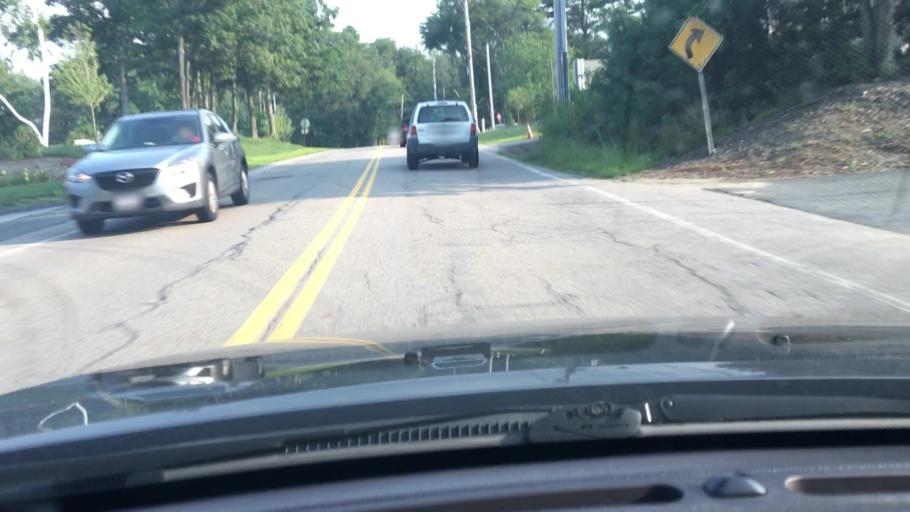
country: US
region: Massachusetts
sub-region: Middlesex County
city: Hopkinton
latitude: 42.1911
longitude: -71.5398
